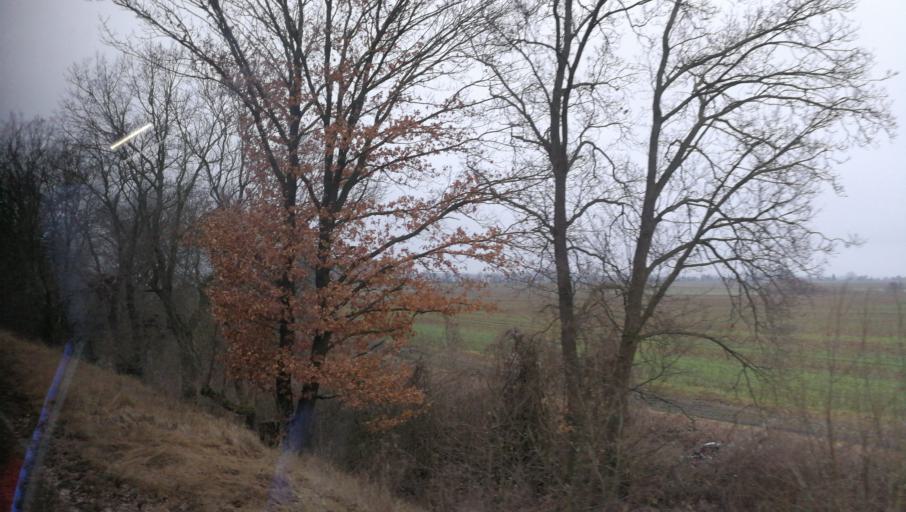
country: DE
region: Mecklenburg-Vorpommern
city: Gross Miltzow
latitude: 53.5193
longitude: 13.5659
